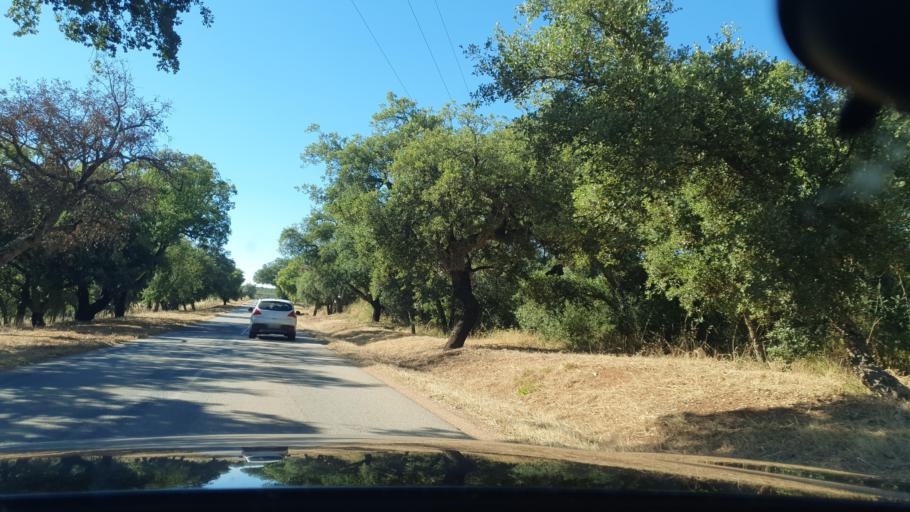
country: PT
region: Evora
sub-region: Vila Vicosa
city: Vila Vicosa
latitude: 38.7446
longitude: -7.4066
